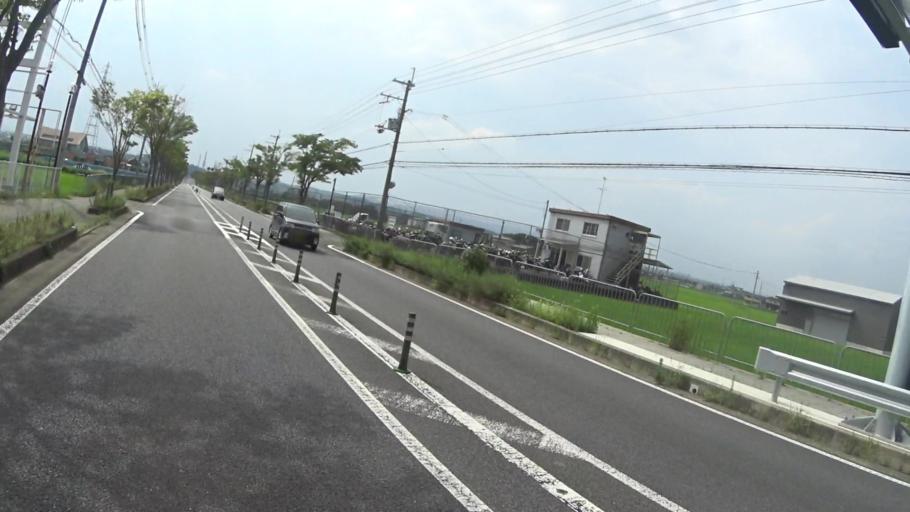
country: JP
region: Nara
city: Nara-shi
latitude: 34.7296
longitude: 135.8157
